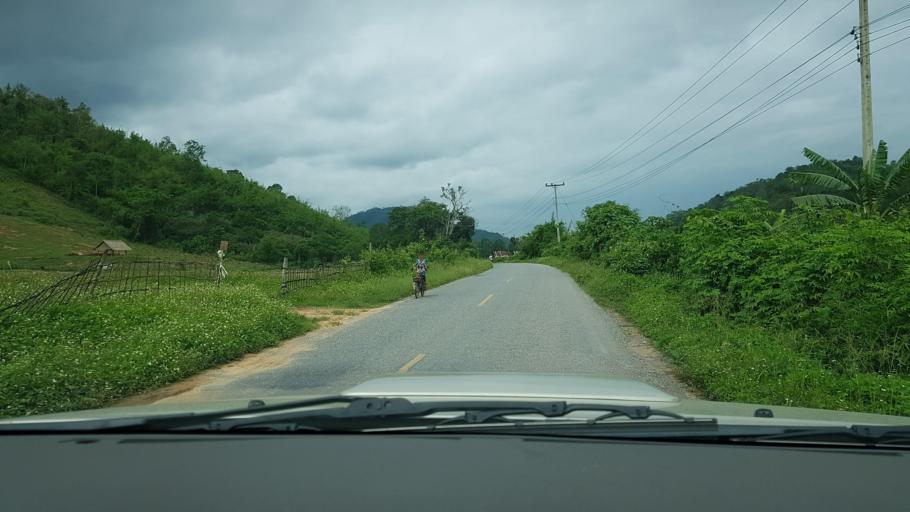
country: LA
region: Loungnamtha
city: Muang Nale
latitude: 20.3973
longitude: 101.7546
